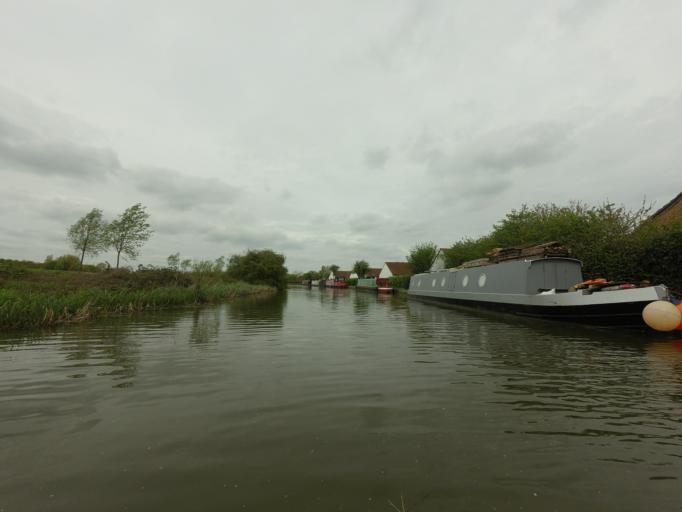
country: GB
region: England
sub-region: Milton Keynes
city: Newport Pagnell
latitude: 52.0712
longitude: -0.7456
